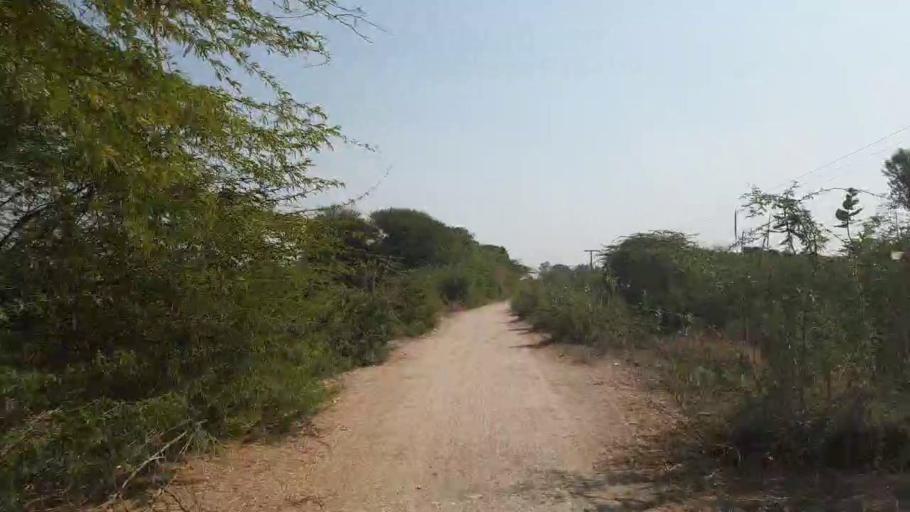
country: PK
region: Sindh
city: Chambar
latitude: 25.4096
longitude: 68.9027
